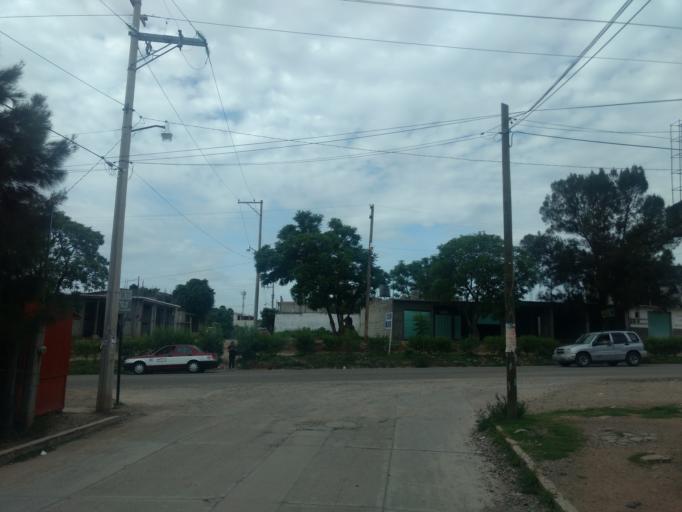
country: MX
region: Oaxaca
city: Ciudad de Huajuapam de Leon
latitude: 17.8035
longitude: -97.7900
